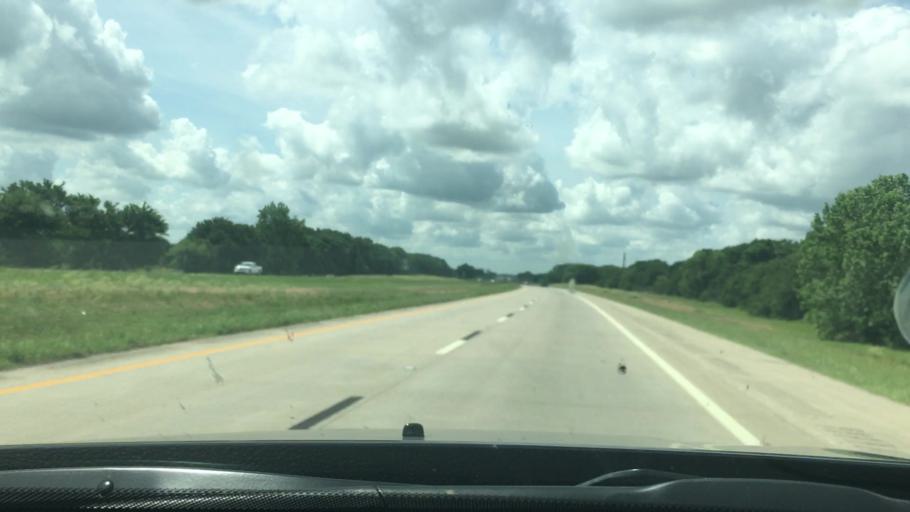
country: US
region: Oklahoma
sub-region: Love County
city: Marietta
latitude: 33.8066
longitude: -97.1350
